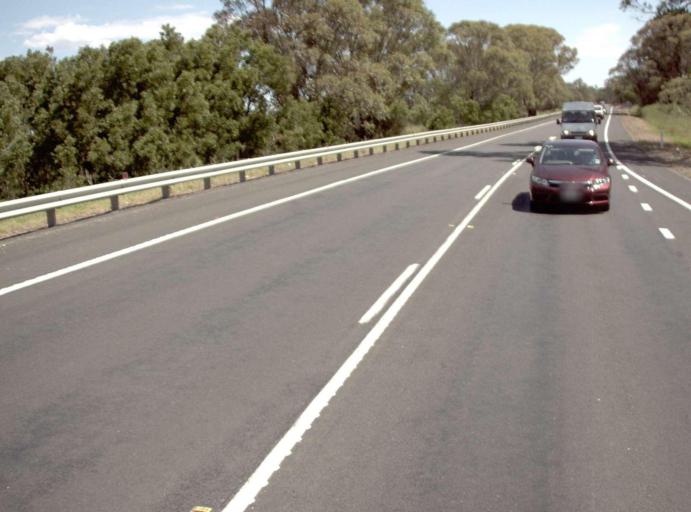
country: AU
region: Victoria
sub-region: Wellington
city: Sale
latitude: -37.9827
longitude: 147.0715
